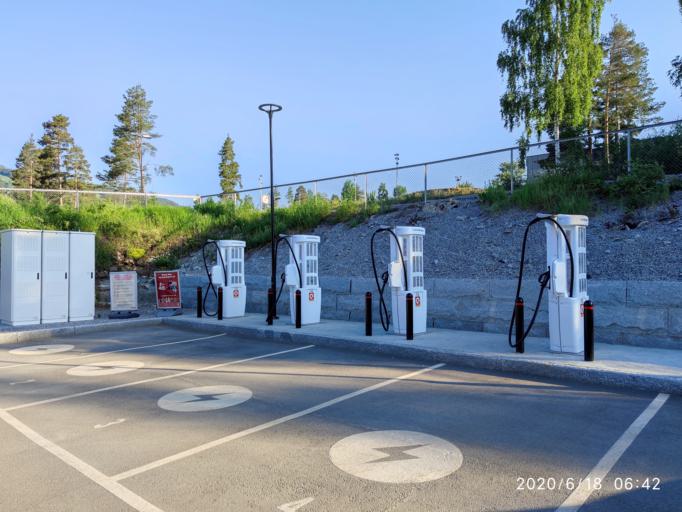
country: NO
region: Buskerud
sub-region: Gol
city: Gol
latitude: 60.7023
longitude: 8.9430
